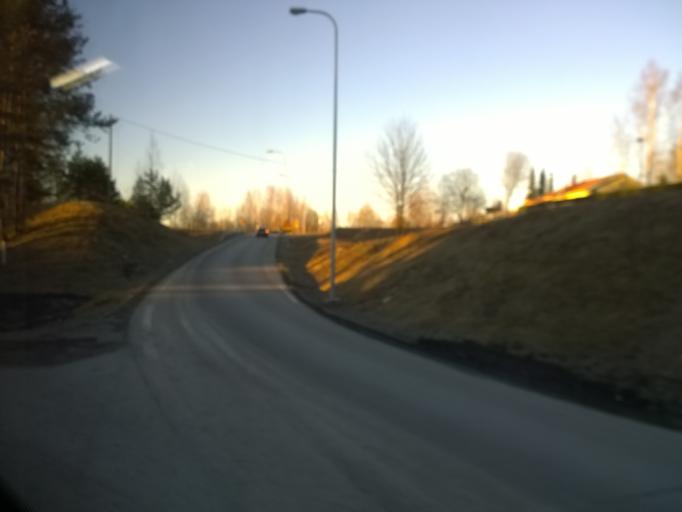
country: FI
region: Pirkanmaa
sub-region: Tampere
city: Tampere
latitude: 61.4778
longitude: 23.8331
